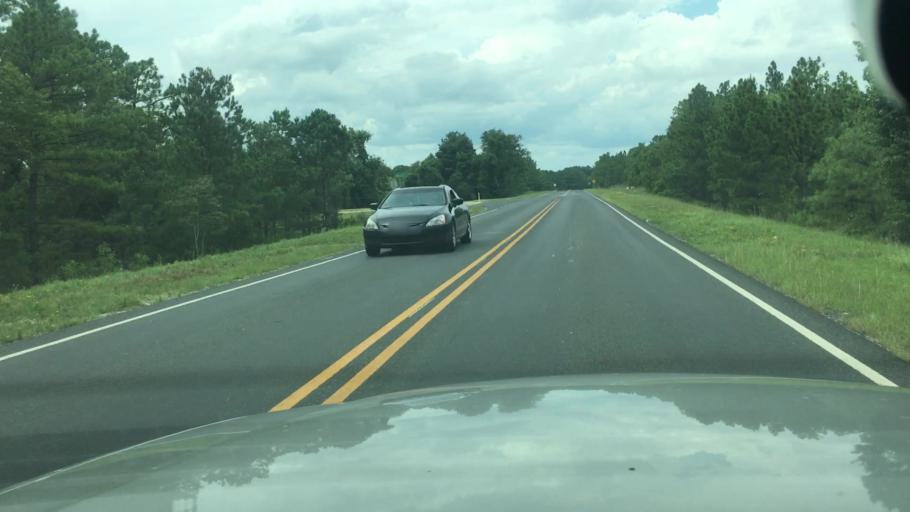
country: US
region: North Carolina
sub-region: Cumberland County
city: Hope Mills
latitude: 34.9708
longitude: -78.8932
